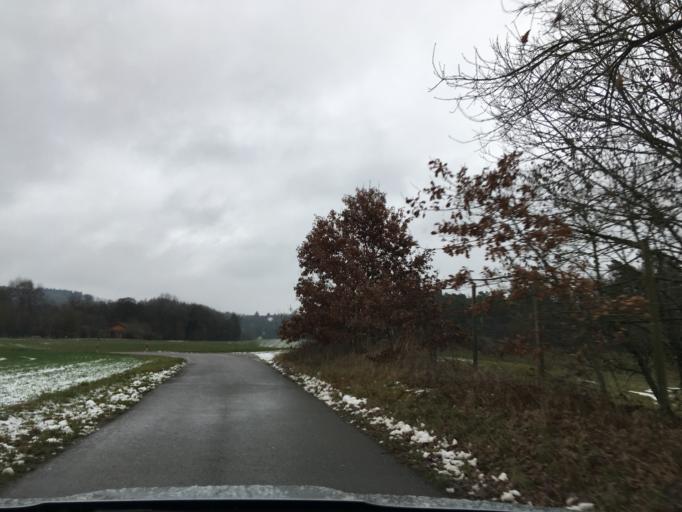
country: DE
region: Baden-Wuerttemberg
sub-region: Freiburg Region
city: Gottmadingen
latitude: 47.7434
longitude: 8.7911
